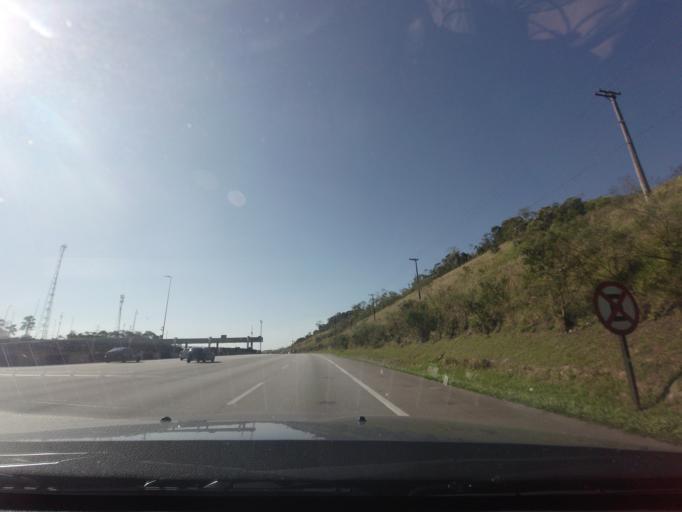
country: BR
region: Sao Paulo
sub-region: Sao Bernardo Do Campo
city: Sao Bernardo do Campo
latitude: -23.8218
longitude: -46.5817
